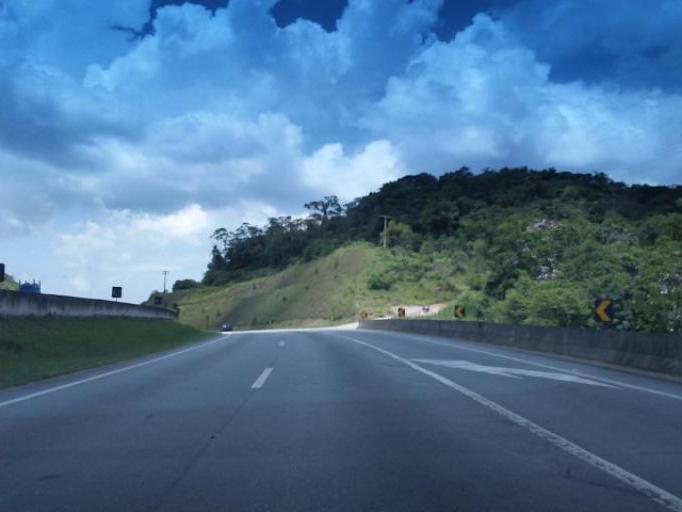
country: BR
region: Sao Paulo
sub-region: Juquitiba
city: Juquitiba
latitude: -24.0109
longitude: -47.1653
